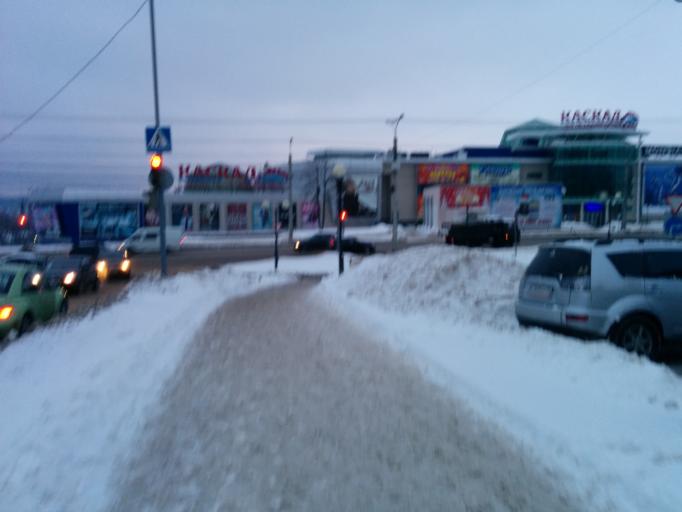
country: RU
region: Chuvashia
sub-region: Cheboksarskiy Rayon
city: Cheboksary
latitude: 56.1347
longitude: 47.2425
